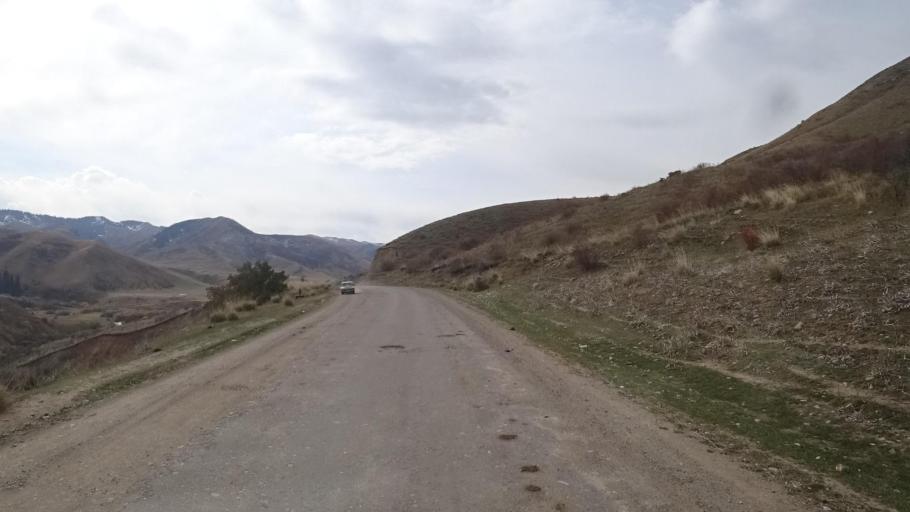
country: KG
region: Ysyk-Koel
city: Teploklyuchenka
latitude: 42.7305
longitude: 78.8238
